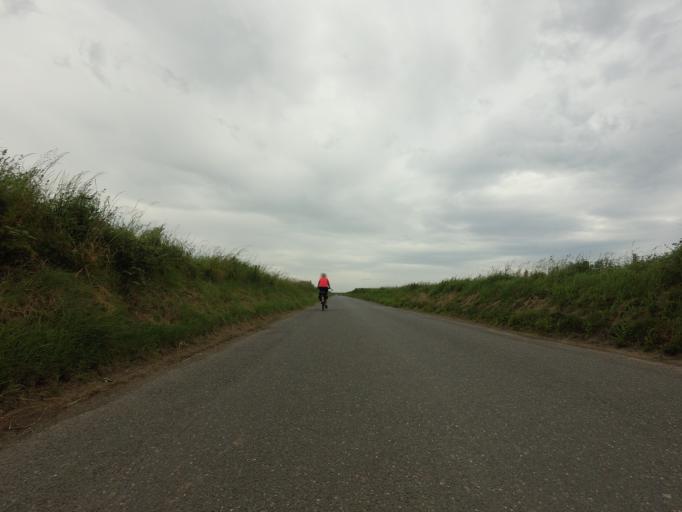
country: GB
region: Scotland
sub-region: Aberdeenshire
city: Whitehills
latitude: 57.6704
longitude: -2.5997
